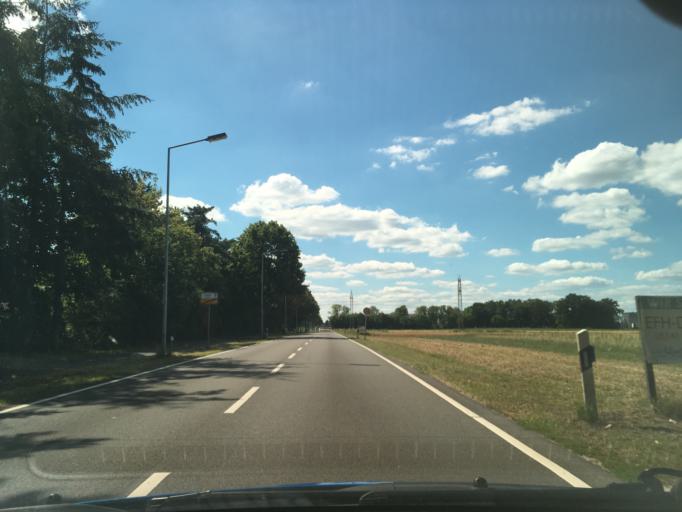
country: DE
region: Lower Saxony
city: Celle
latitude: 52.6053
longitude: 10.1129
